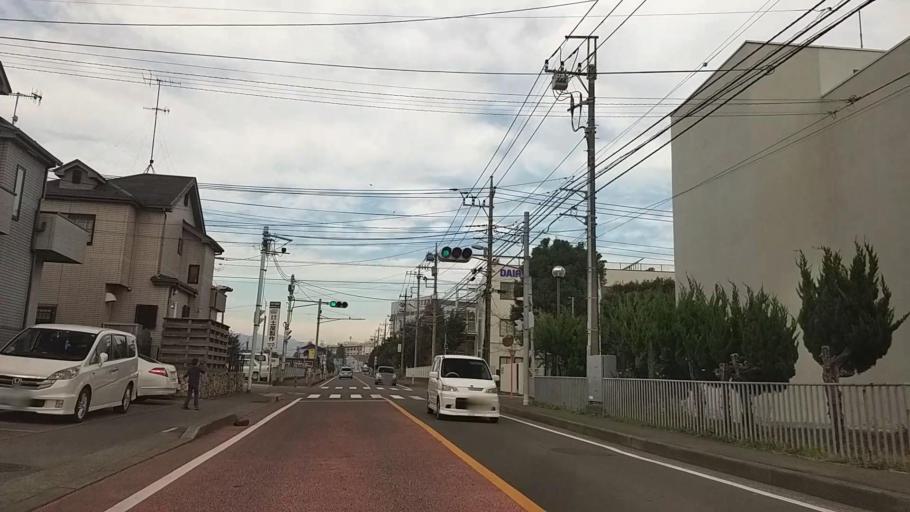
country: JP
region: Kanagawa
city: Fujisawa
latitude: 35.4002
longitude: 139.4263
